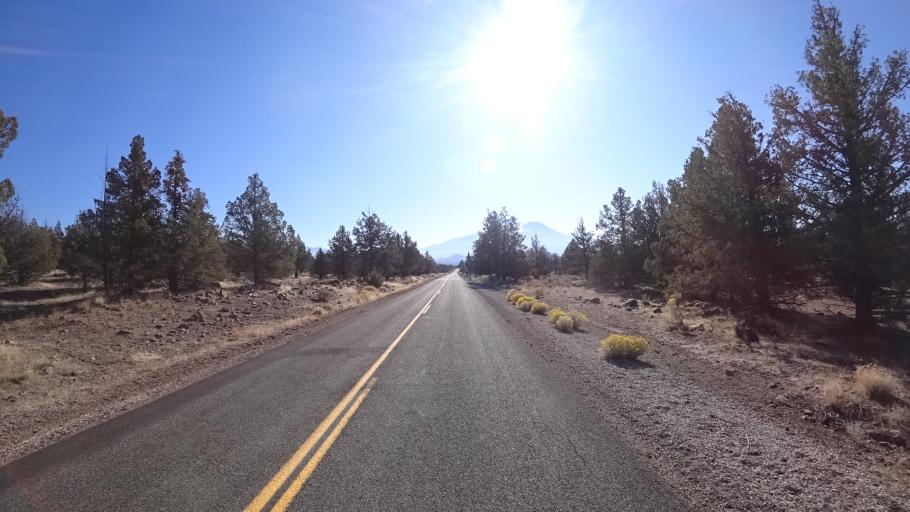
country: US
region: California
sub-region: Siskiyou County
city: Weed
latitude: 41.6104
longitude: -122.3119
